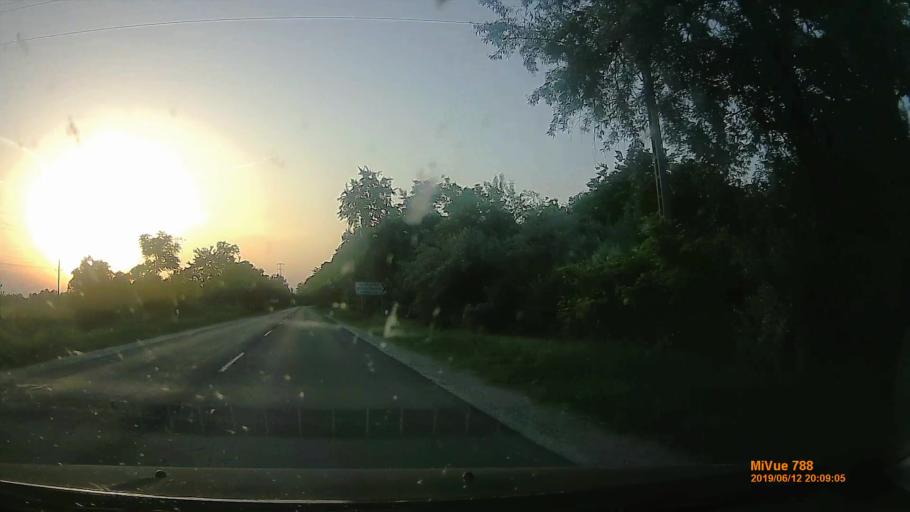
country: HU
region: Pest
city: Ocsa
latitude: 47.2532
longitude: 19.2267
